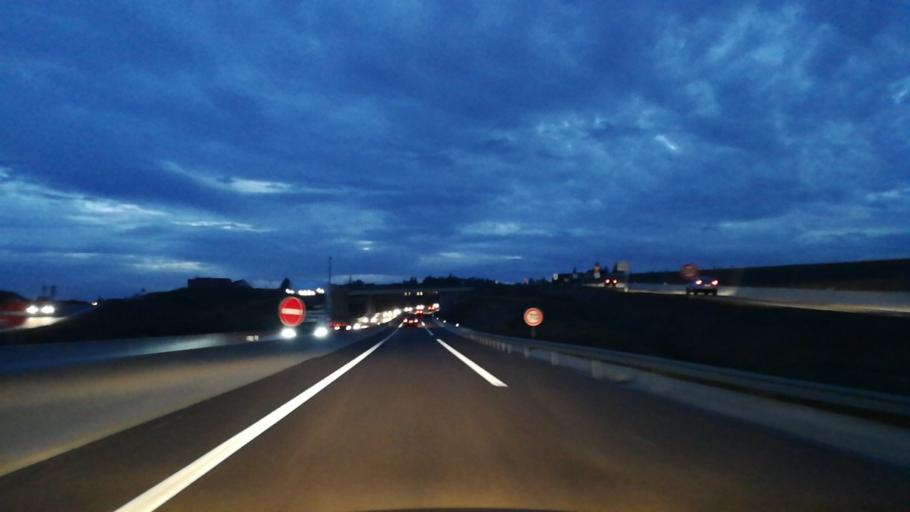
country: FR
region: Bourgogne
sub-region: Departement de la Cote-d'Or
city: Daix
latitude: 47.3482
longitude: 5.0090
